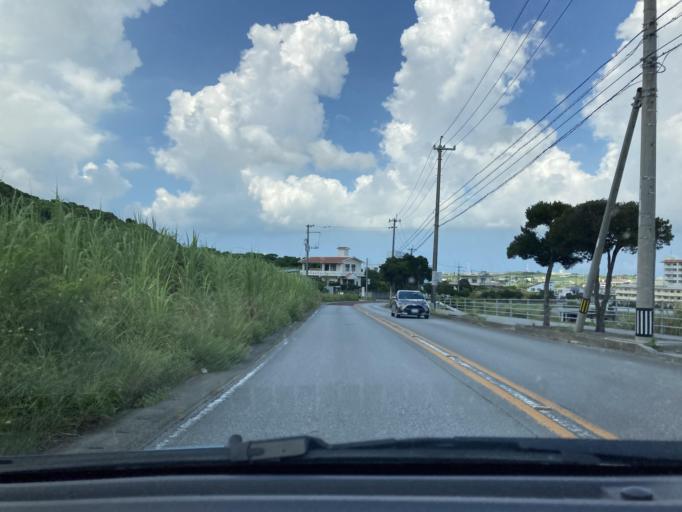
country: JP
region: Okinawa
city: Tomigusuku
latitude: 26.1493
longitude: 127.7545
